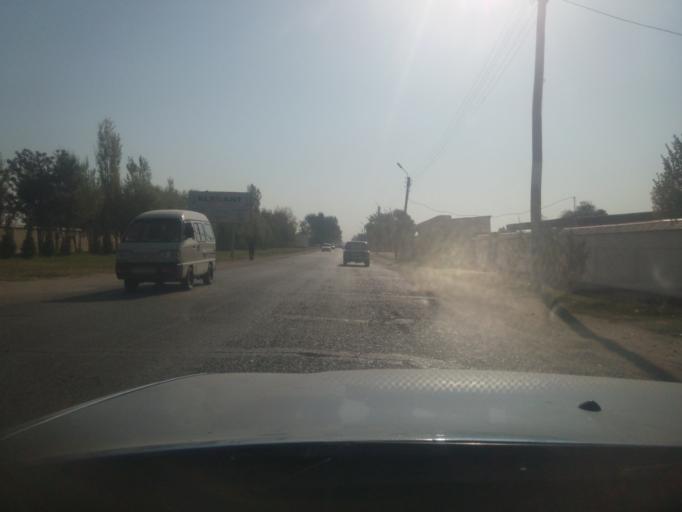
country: UZ
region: Sirdaryo
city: Guliston
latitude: 40.4947
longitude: 68.7925
